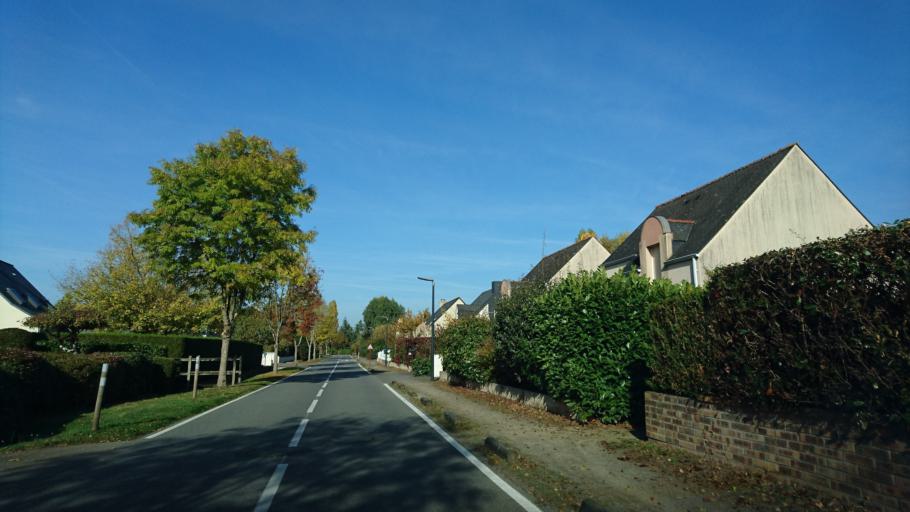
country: FR
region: Brittany
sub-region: Departement d'Ille-et-Vilaine
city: Bruz
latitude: 48.0340
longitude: -1.7678
